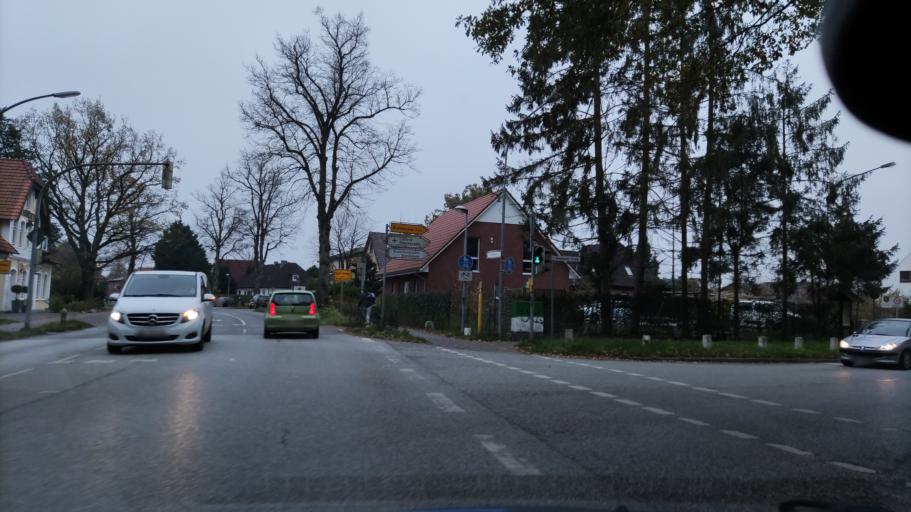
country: DE
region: Schleswig-Holstein
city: Gross Gronau
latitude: 53.8233
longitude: 10.7222
